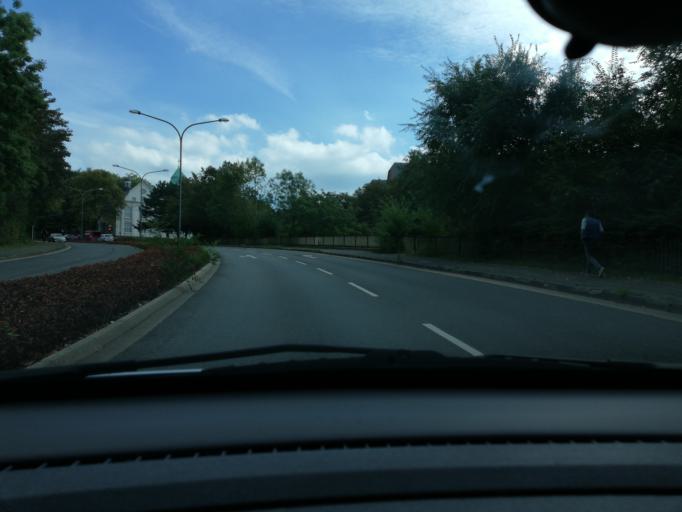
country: DE
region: North Rhine-Westphalia
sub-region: Regierungsbezirk Dusseldorf
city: Wuppertal
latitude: 51.2689
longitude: 7.1514
